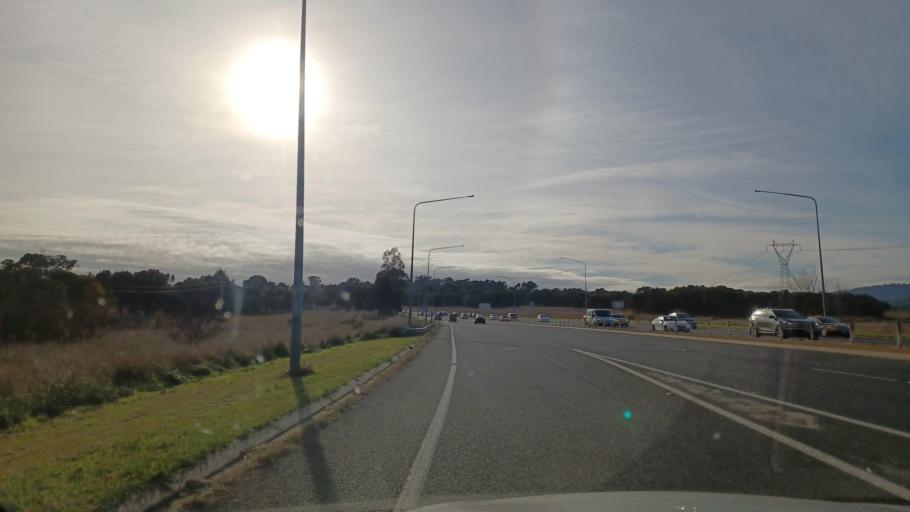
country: AU
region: Australian Capital Territory
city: Kaleen
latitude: -35.2244
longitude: 149.1249
